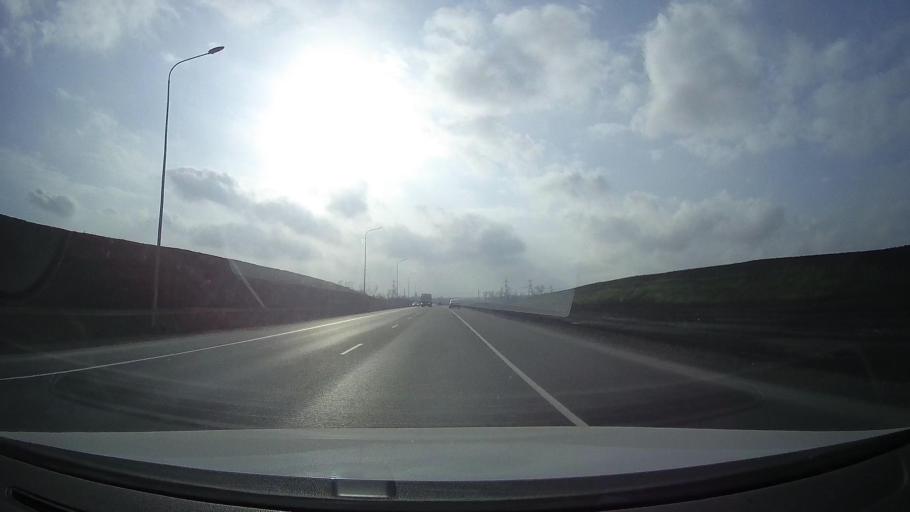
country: RU
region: Rostov
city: Grushevskaya
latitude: 47.4156
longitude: 39.8607
